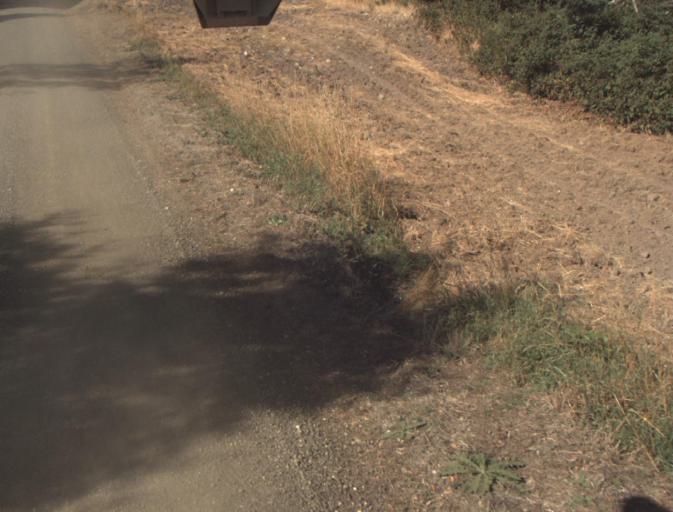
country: AU
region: Tasmania
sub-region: Launceston
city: Mayfield
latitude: -41.1686
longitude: 147.2116
